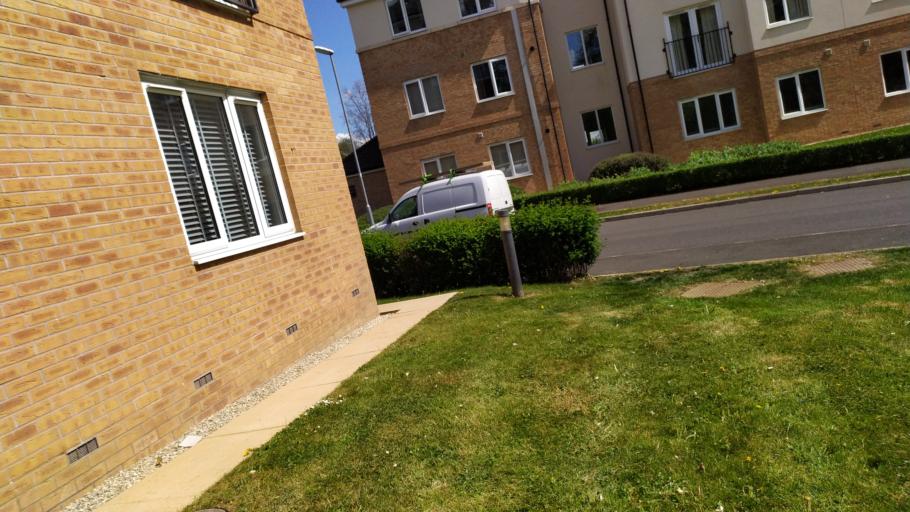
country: GB
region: England
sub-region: City and Borough of Leeds
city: Shadwell
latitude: 53.8090
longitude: -1.4776
